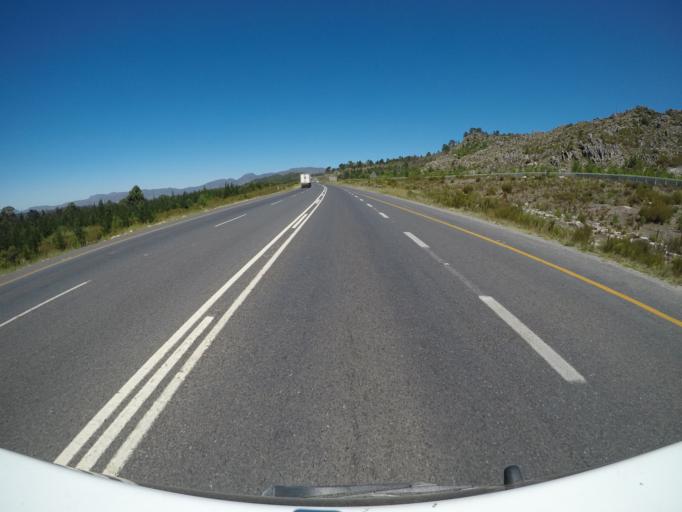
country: ZA
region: Western Cape
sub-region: Overberg District Municipality
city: Grabouw
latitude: -34.1636
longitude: 19.0070
